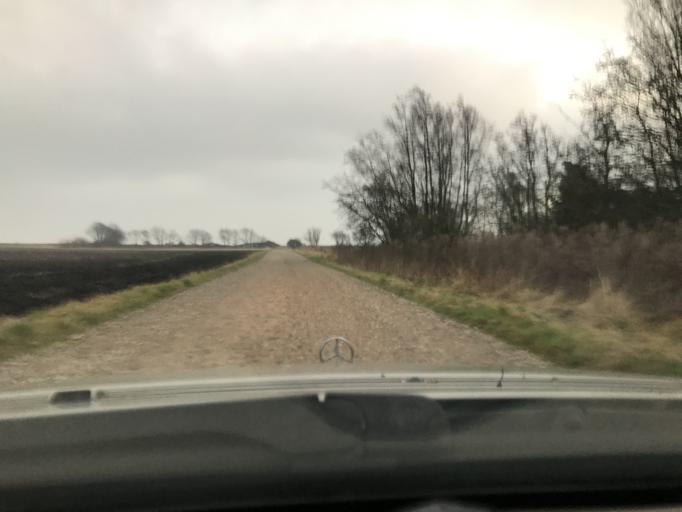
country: DK
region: South Denmark
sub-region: Sonderborg Kommune
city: Horuphav
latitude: 54.8684
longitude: 10.0026
